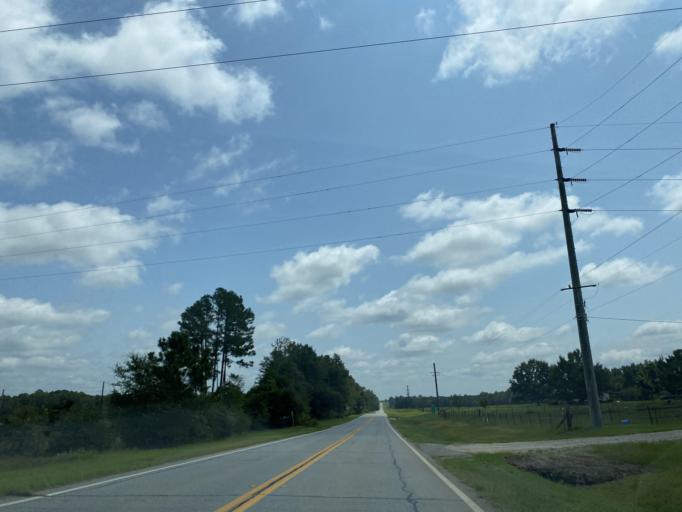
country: US
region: Georgia
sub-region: Wilcox County
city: Abbeville
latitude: 32.0088
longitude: -83.1186
